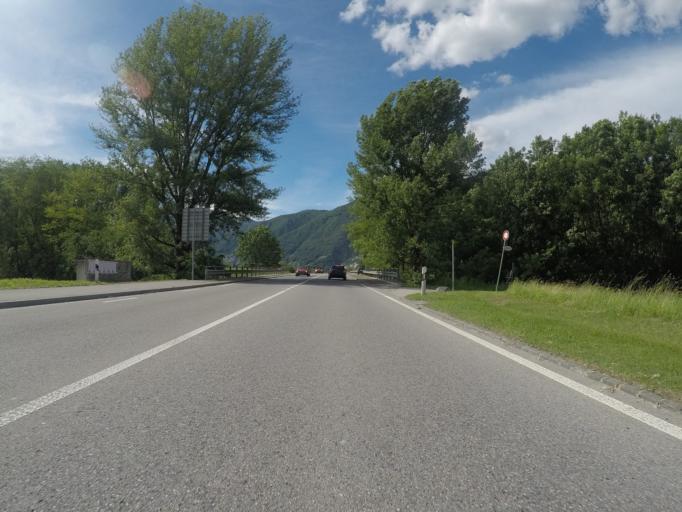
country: CH
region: Ticino
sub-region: Locarno District
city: Cugnasco
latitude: 46.1560
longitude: 8.8900
